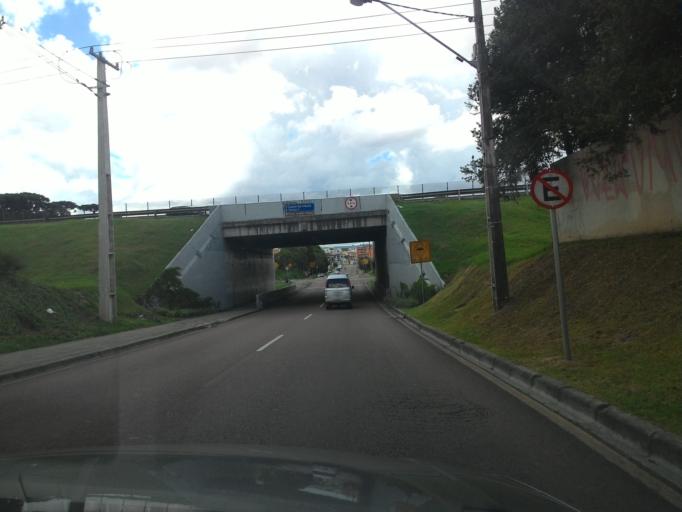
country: BR
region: Parana
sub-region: Pinhais
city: Pinhais
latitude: -25.4520
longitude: -49.2279
